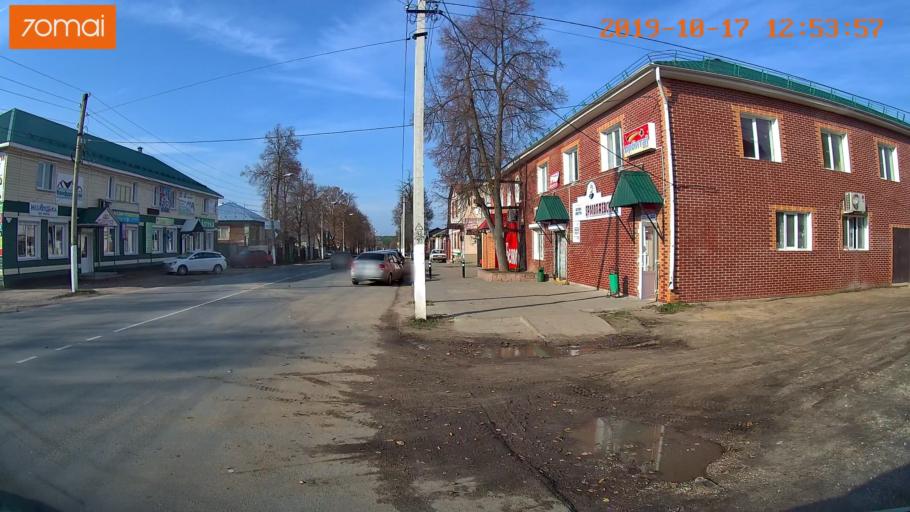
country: RU
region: Rjazan
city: Kasimov
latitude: 54.9422
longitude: 41.3802
